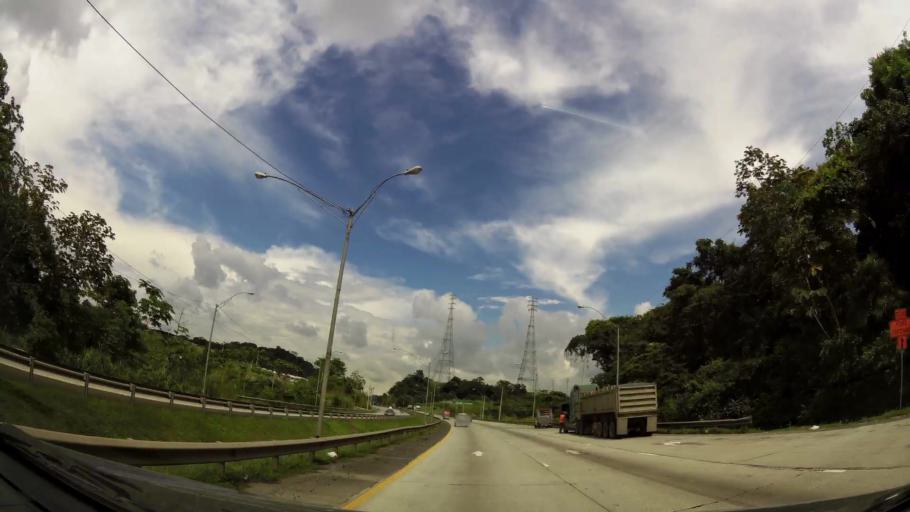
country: PA
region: Panama
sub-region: Distrito de Panama
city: Paraiso
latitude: 9.0204
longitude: -79.6400
